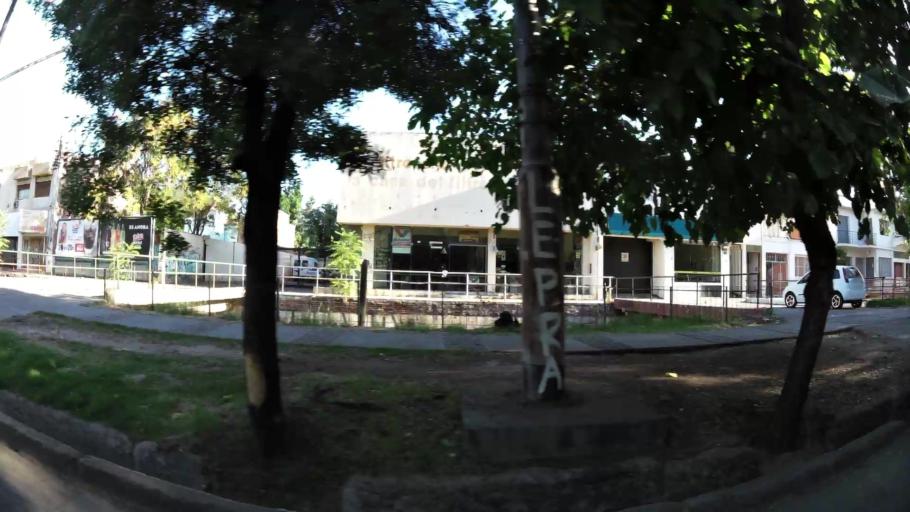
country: AR
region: Mendoza
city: Mendoza
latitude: -32.8994
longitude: -68.8394
